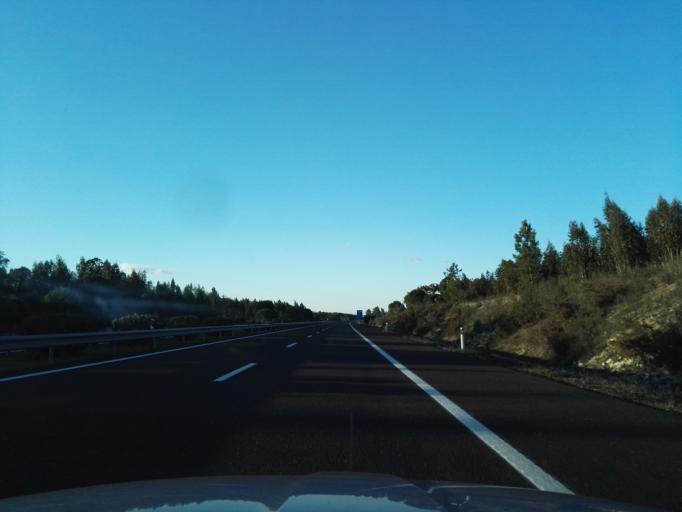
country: PT
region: Santarem
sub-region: Benavente
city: Poceirao
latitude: 38.8145
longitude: -8.7085
